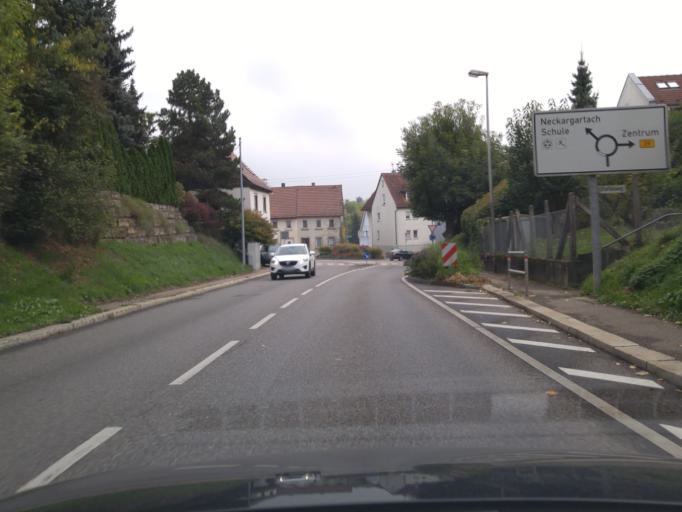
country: DE
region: Baden-Wuerttemberg
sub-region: Regierungsbezirk Stuttgart
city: Heilbronn
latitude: 49.1616
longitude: 9.1721
